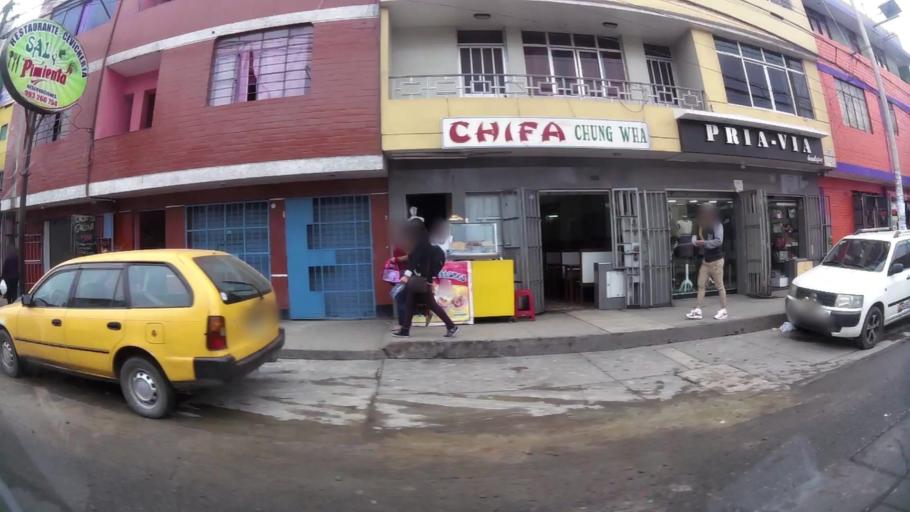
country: PE
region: Lima
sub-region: Lima
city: Surco
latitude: -12.1543
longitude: -76.9524
